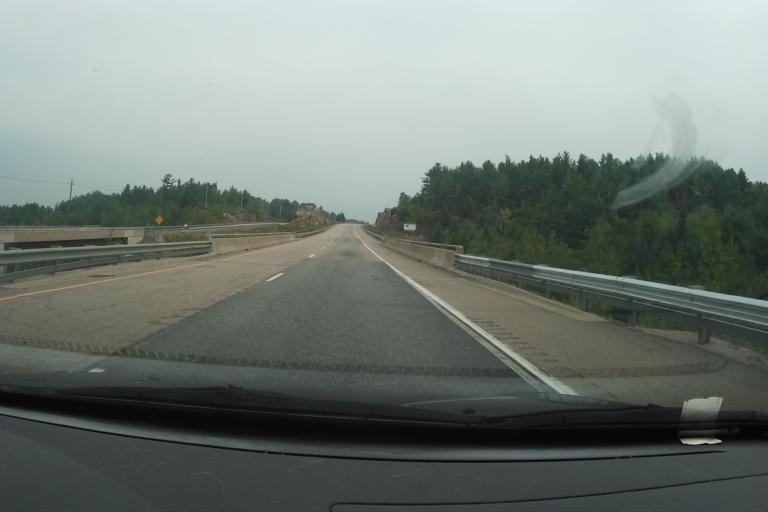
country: CA
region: Ontario
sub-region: Nipissing District
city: North Bay
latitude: 46.2097
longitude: -79.3489
